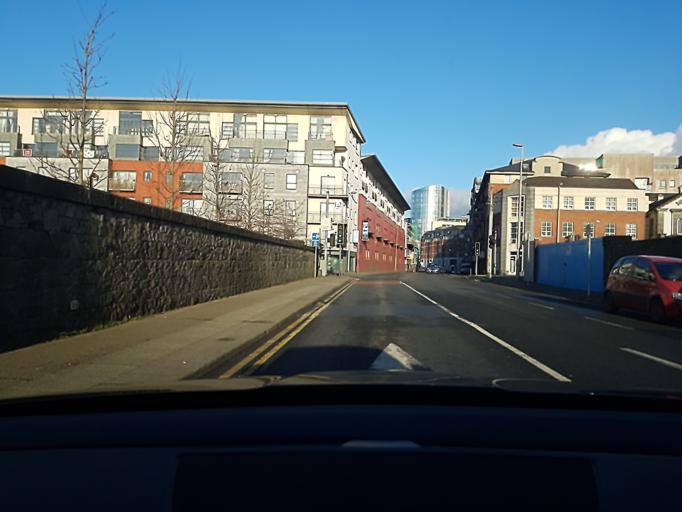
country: IE
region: Munster
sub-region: County Limerick
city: Luimneach
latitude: 52.6594
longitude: -8.6375
